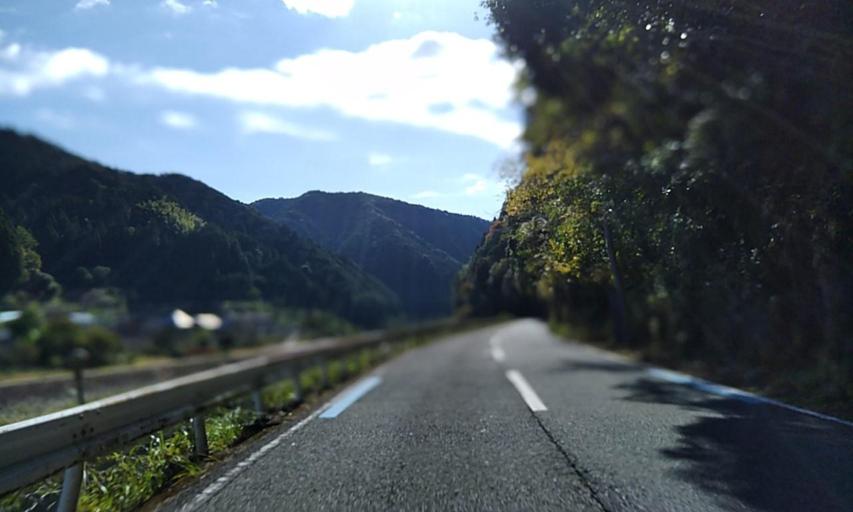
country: JP
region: Wakayama
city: Kainan
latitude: 34.0685
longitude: 135.3554
